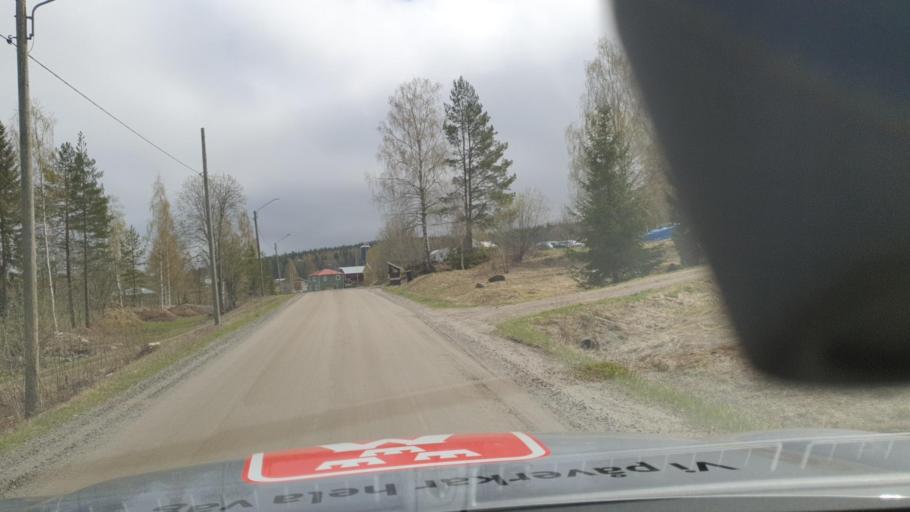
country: SE
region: Vaesterbotten
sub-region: Bjurholms Kommun
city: Bjurholm
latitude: 63.6708
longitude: 19.0002
